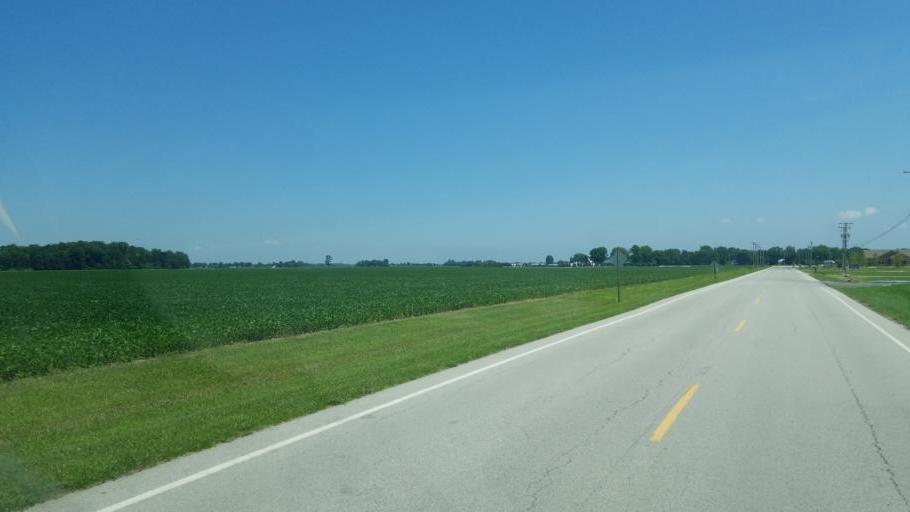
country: US
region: Ohio
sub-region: Sandusky County
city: Fremont
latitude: 41.3668
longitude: -83.0908
